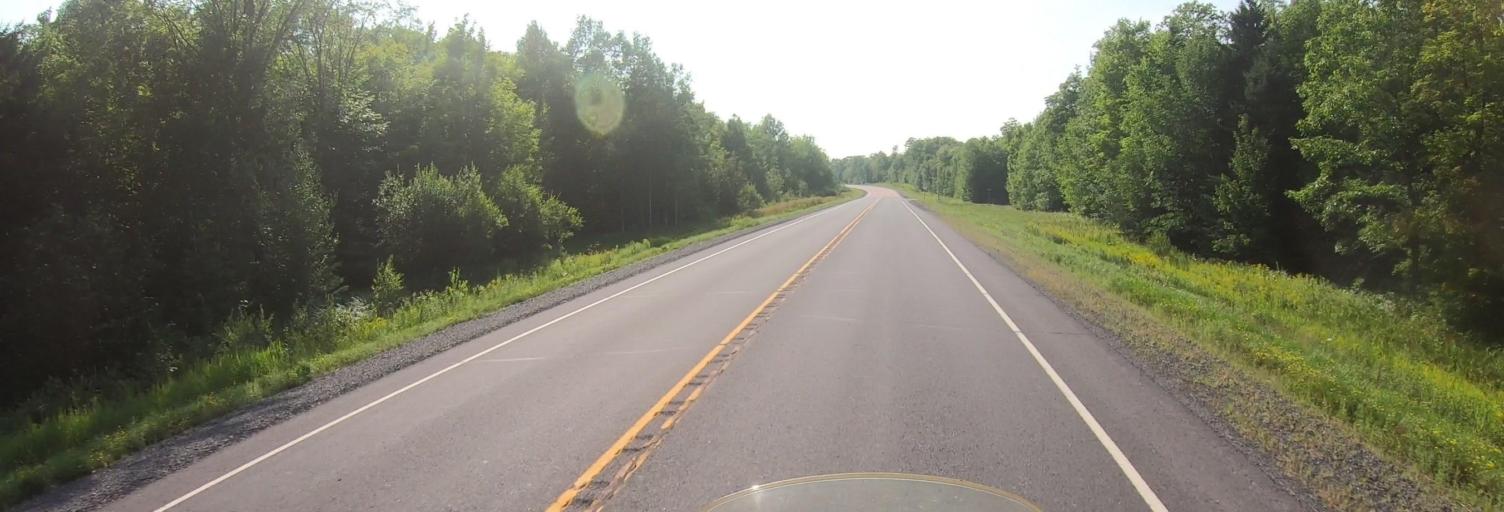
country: US
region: Wisconsin
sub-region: Iron County
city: Hurley
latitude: 46.3671
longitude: -90.4173
